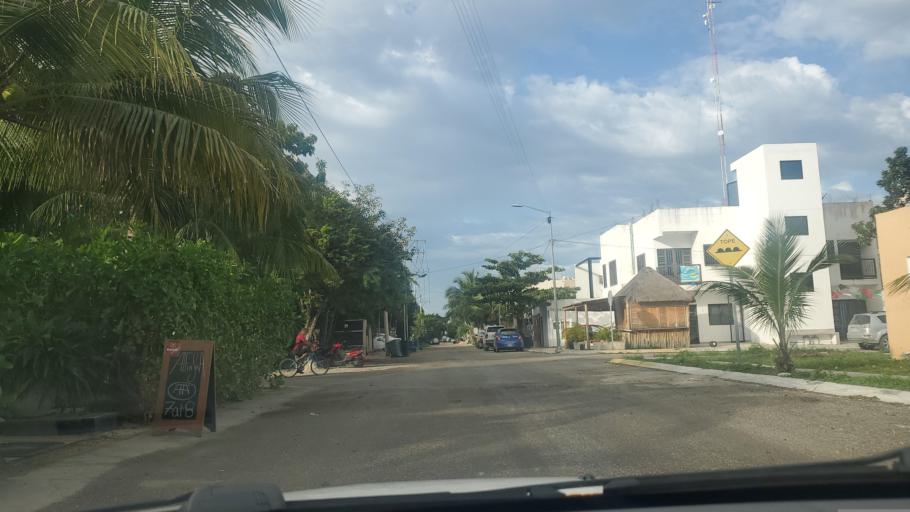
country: MX
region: Quintana Roo
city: Tulum
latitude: 20.2152
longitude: -87.4550
